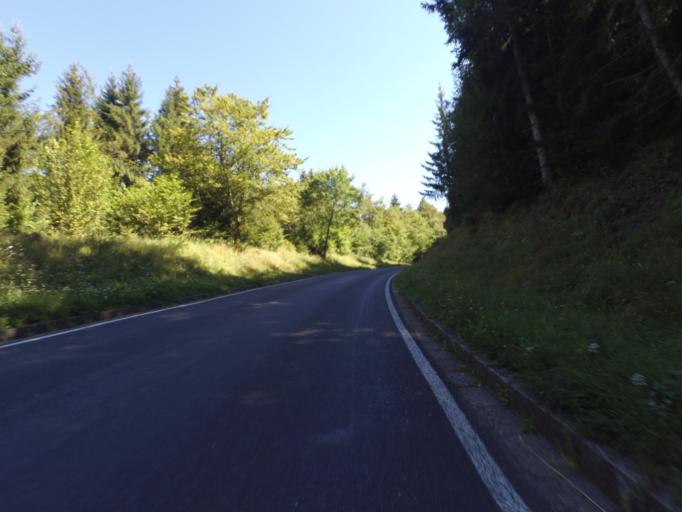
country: DE
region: Rheinland-Pfalz
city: Nohn
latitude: 50.3068
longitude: 6.7894
